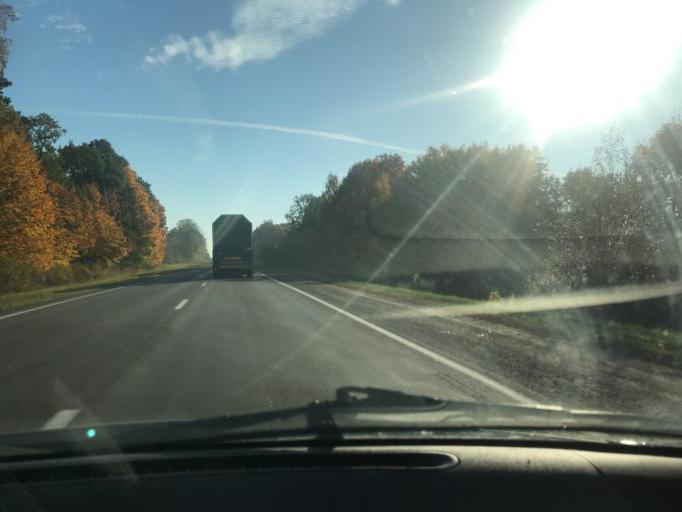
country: BY
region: Brest
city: Ivanava
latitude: 52.1503
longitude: 25.3871
